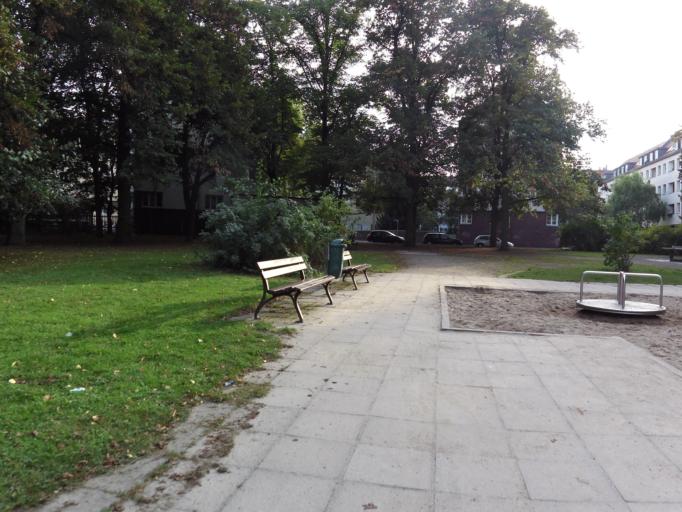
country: DE
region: Saxony
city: Leipzig
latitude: 51.3271
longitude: 12.4096
